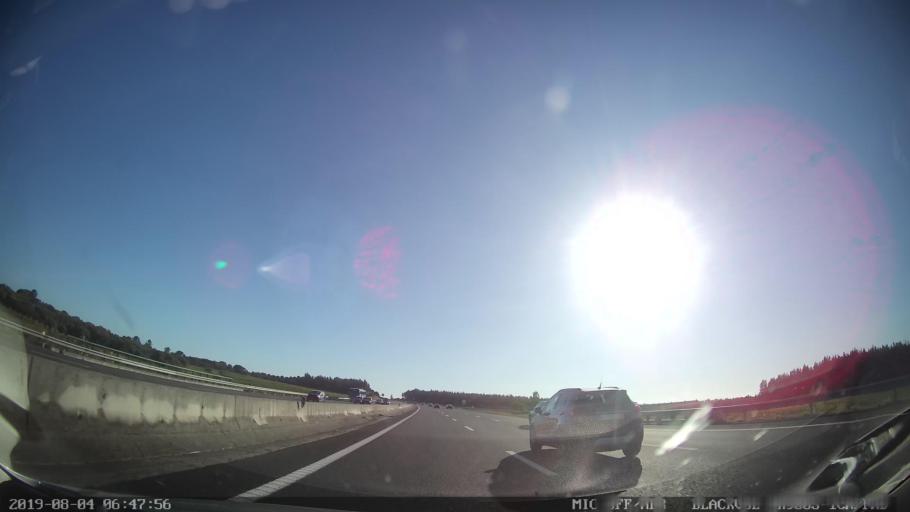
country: PT
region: Santarem
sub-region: Cartaxo
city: Cartaxo
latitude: 39.1975
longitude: -8.8067
